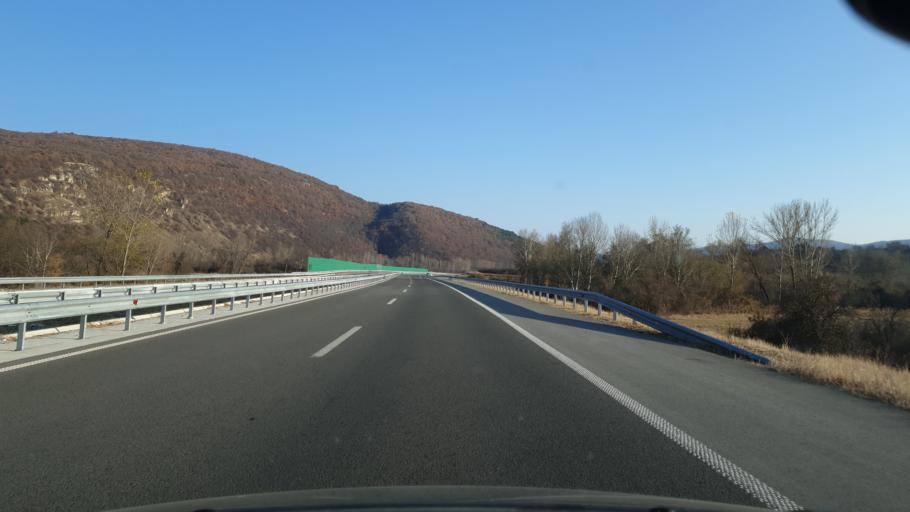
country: RS
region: Central Serbia
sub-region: Pirotski Okrug
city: Dimitrovgrad
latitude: 43.0374
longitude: 22.7144
